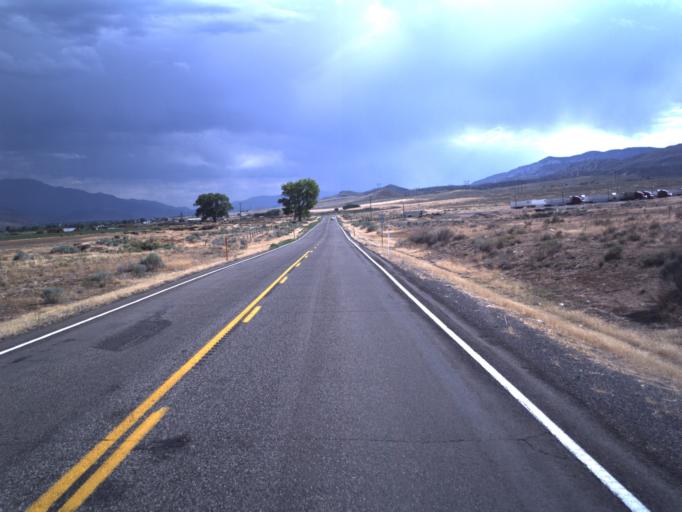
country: US
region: Utah
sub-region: Sevier County
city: Aurora
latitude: 38.9554
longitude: -111.9291
